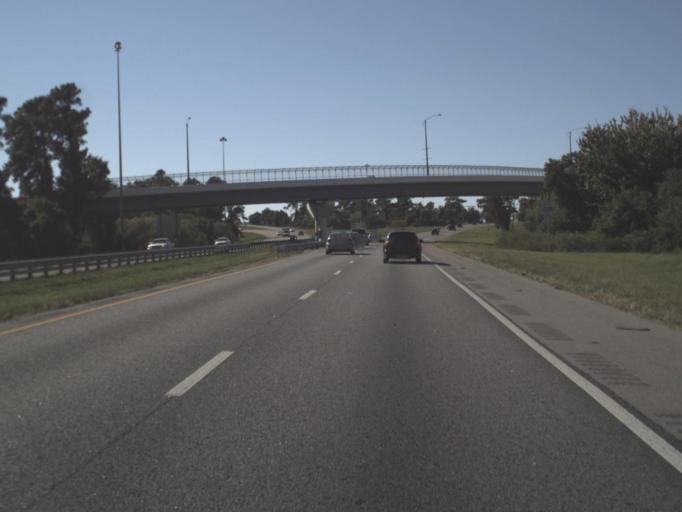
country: US
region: Florida
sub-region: Orange County
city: Williamsburg
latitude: 28.4211
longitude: -81.4659
